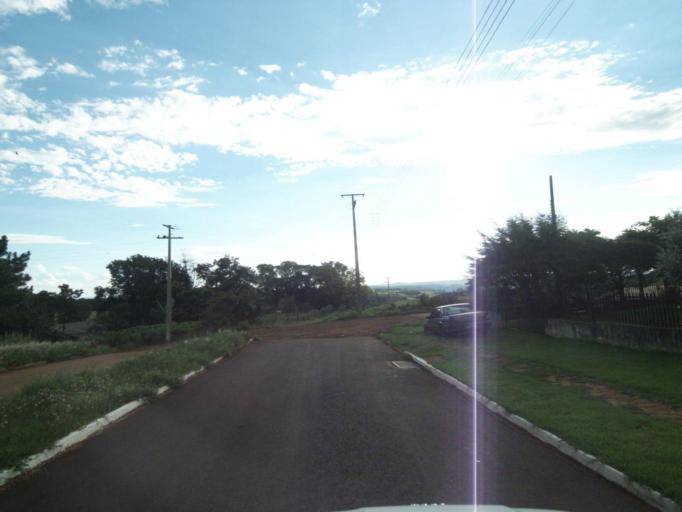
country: BR
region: Parana
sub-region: Laranjeiras Do Sul
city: Laranjeiras do Sul
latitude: -25.4957
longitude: -52.5348
